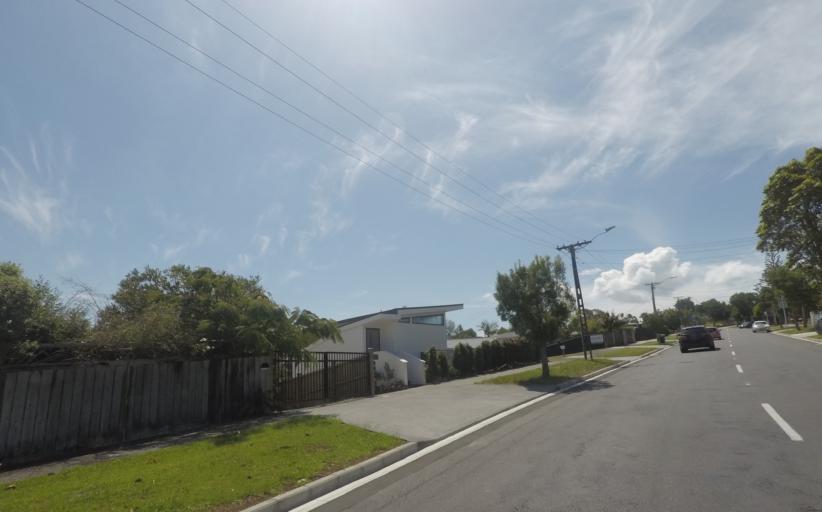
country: NZ
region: Auckland
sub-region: Auckland
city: Tamaki
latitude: -36.8700
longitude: 174.8499
